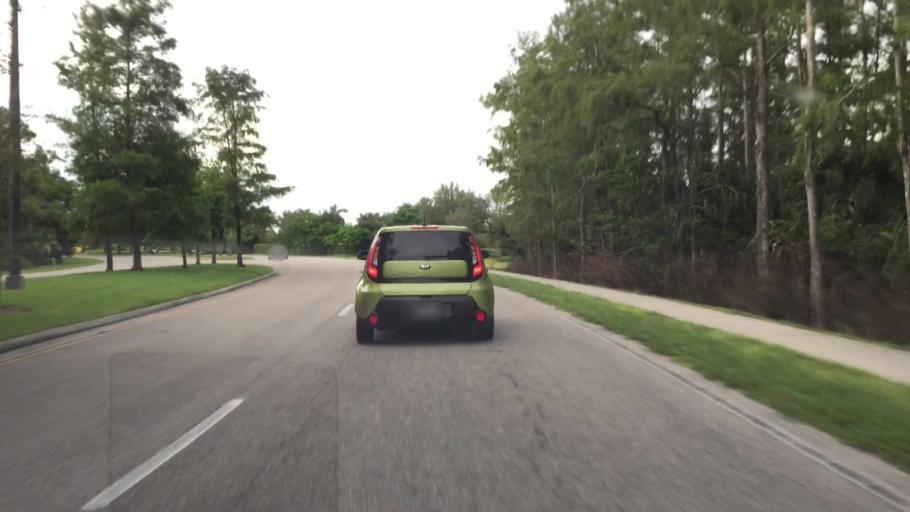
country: US
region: Florida
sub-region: Lee County
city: Fort Myers
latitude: 26.6227
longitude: -81.7931
